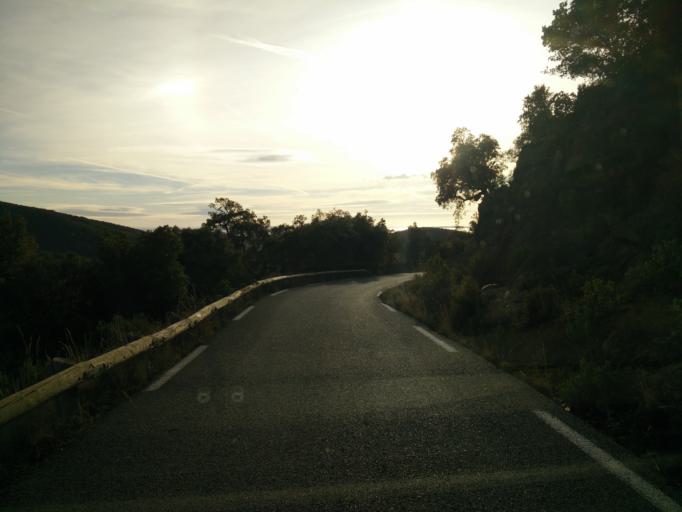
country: FR
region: Provence-Alpes-Cote d'Azur
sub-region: Departement du Var
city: Bormes-les-Mimosas
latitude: 43.1853
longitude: 6.3405
